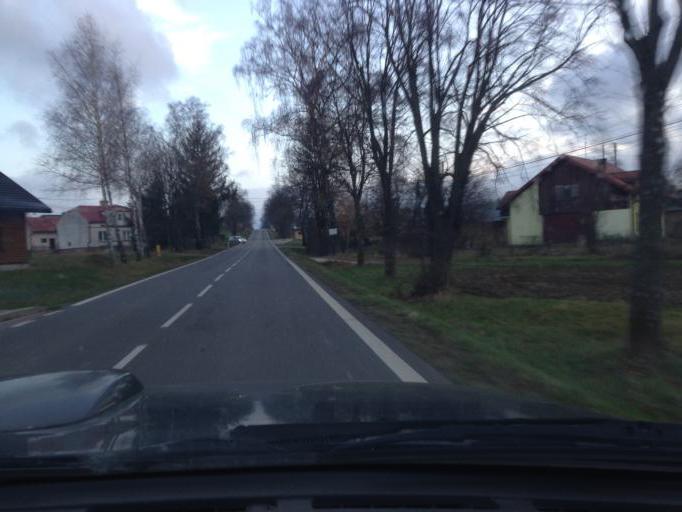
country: PL
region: Subcarpathian Voivodeship
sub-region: Powiat jasielski
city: Nowy Zmigrod
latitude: 49.6327
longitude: 21.5280
